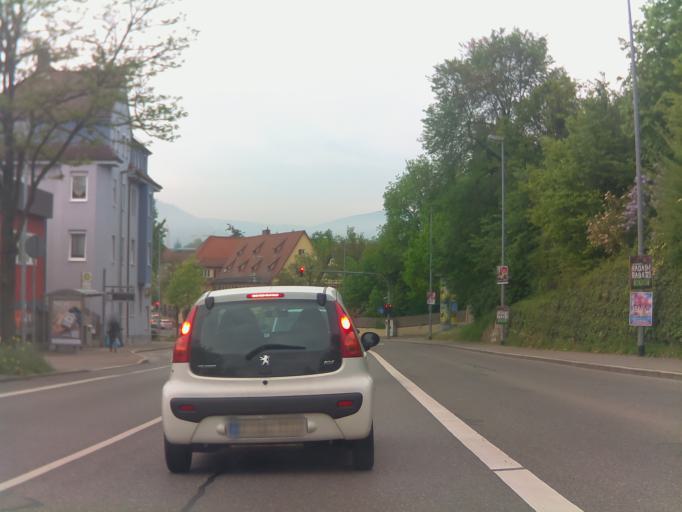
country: DE
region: Baden-Wuerttemberg
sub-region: Tuebingen Region
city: Reutlingen
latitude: 48.4992
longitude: 9.2045
